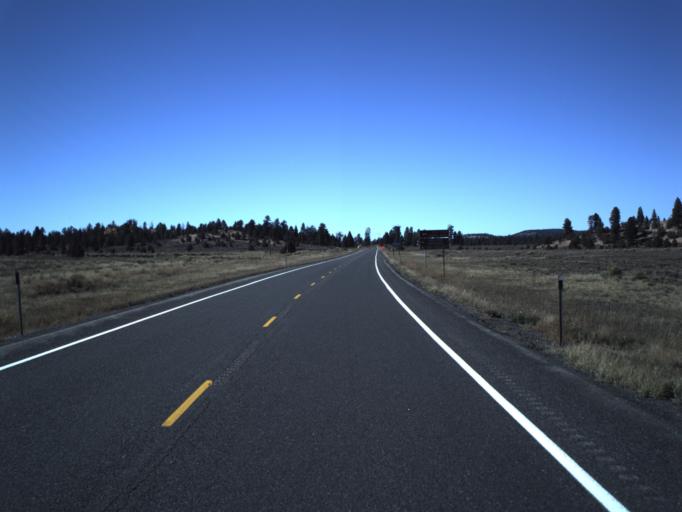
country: US
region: Utah
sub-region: Garfield County
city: Panguitch
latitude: 37.7019
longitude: -112.1976
